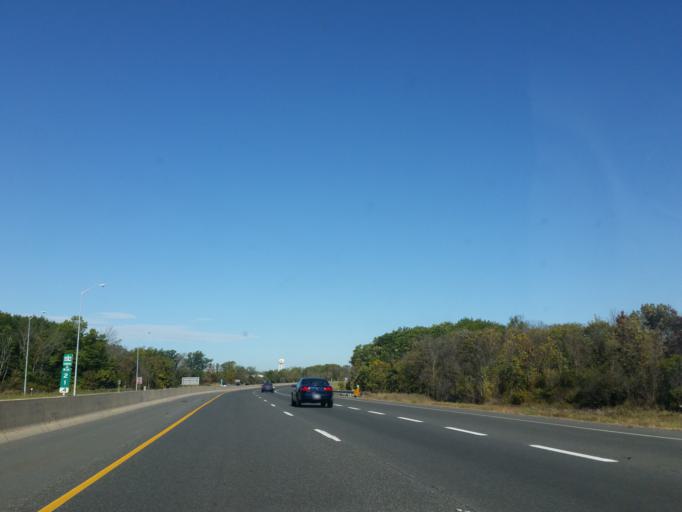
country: CA
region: Ontario
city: Niagara Falls
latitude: 43.0345
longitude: -79.1151
